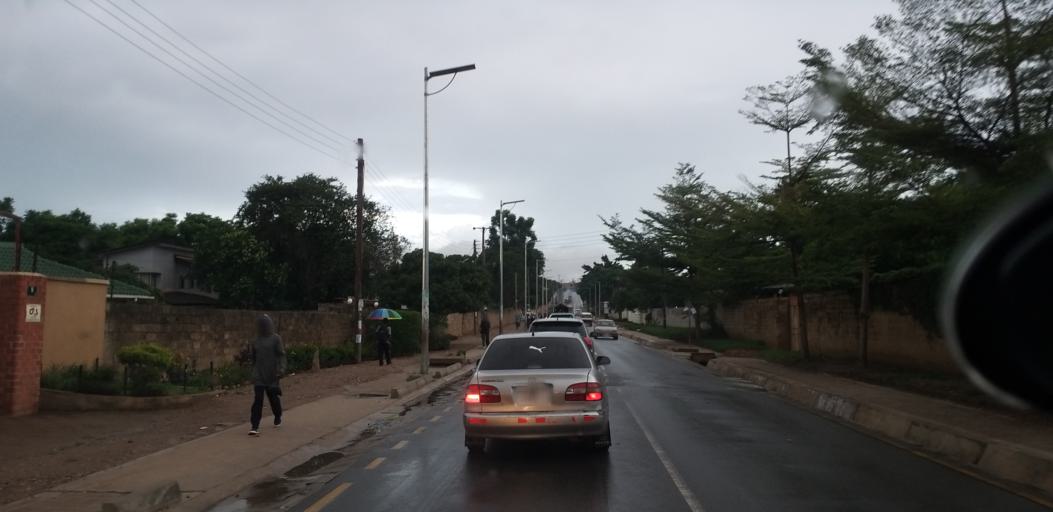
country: ZM
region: Lusaka
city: Lusaka
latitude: -15.4175
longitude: 28.3587
